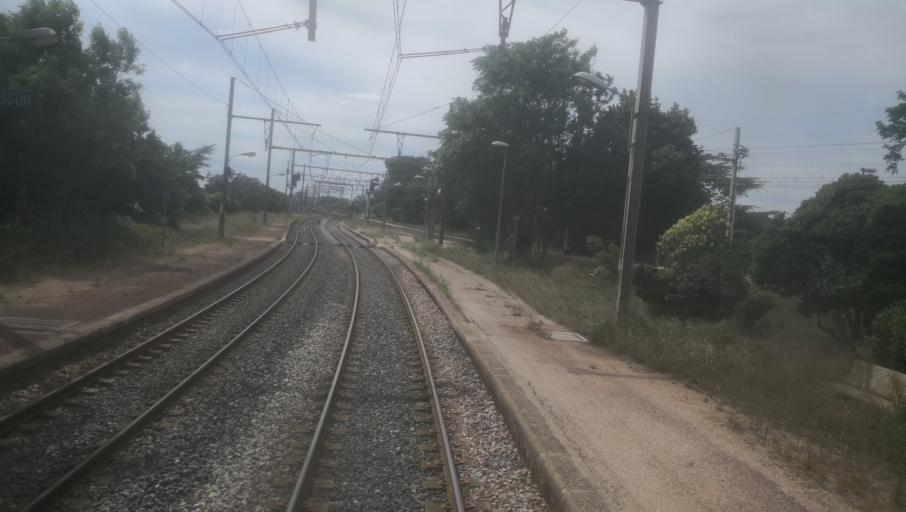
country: FR
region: Provence-Alpes-Cote d'Azur
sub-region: Departement des Bouches-du-Rhone
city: Tarascon
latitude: 43.8010
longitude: 4.6565
